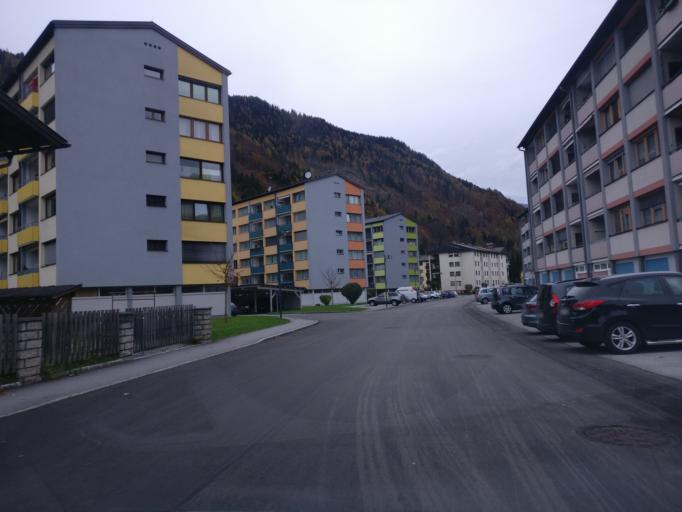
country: AT
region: Salzburg
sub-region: Politischer Bezirk Sankt Johann im Pongau
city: Bischofshofen
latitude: 47.4279
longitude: 13.2163
